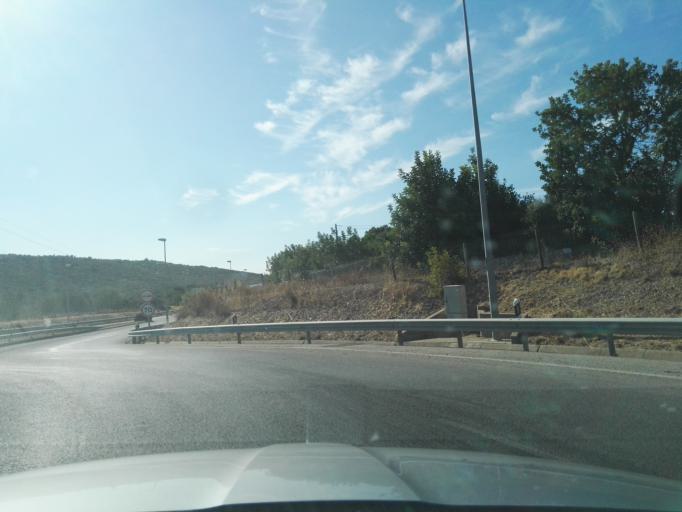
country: PT
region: Faro
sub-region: Sao Bras de Alportel
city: Sao Bras de Alportel
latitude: 37.1469
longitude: -7.9020
